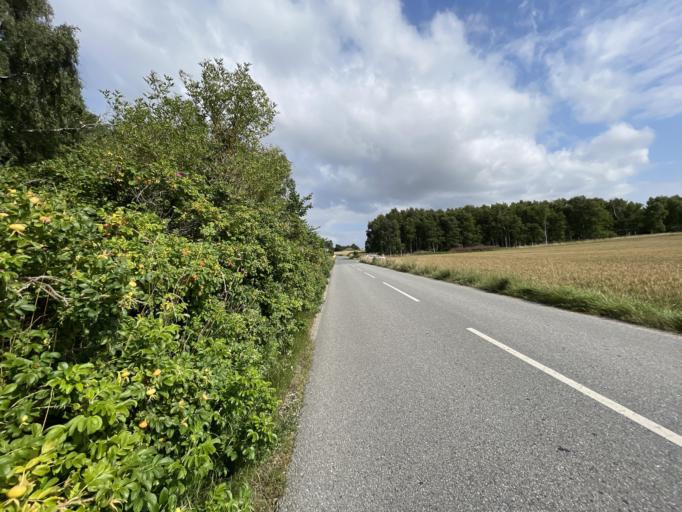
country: DK
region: Capital Region
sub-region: Gribskov Kommune
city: Helsinge
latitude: 56.0902
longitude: 12.1765
